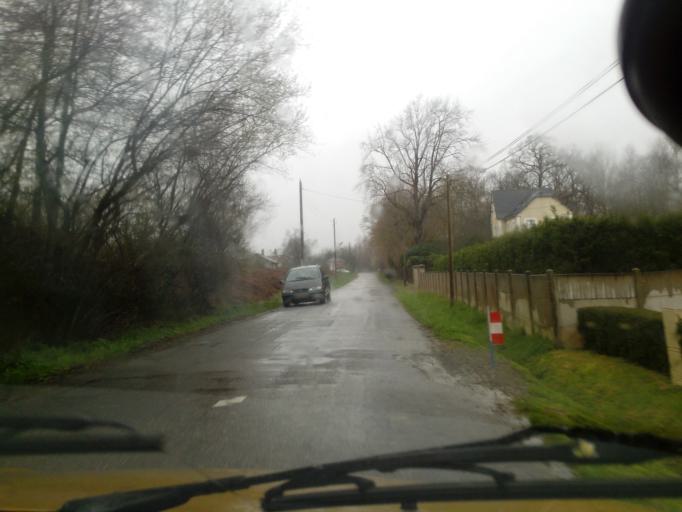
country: FR
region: Brittany
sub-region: Departement d'Ille-et-Vilaine
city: Saint-Medard-sur-Ille
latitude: 48.2386
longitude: -1.6512
